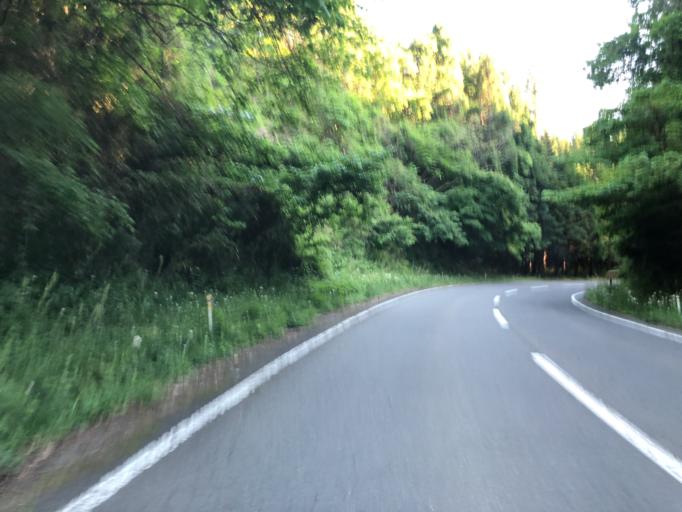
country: JP
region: Ibaraki
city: Daigo
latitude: 36.9260
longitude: 140.4626
